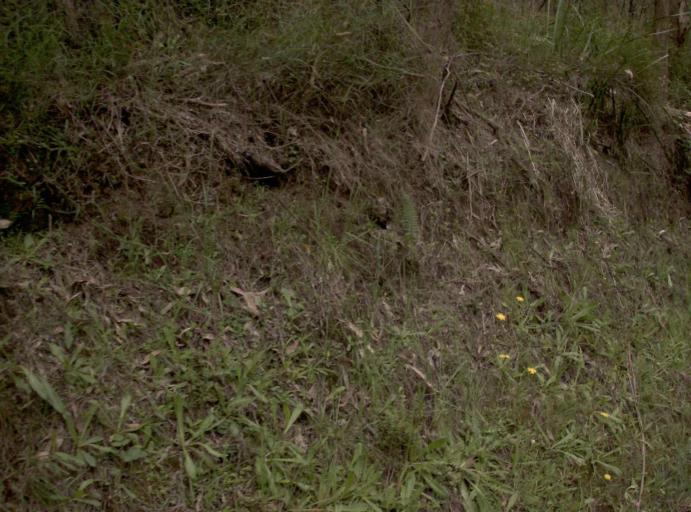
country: AU
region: Victoria
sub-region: Baw Baw
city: Warragul
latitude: -37.8906
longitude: 146.0879
